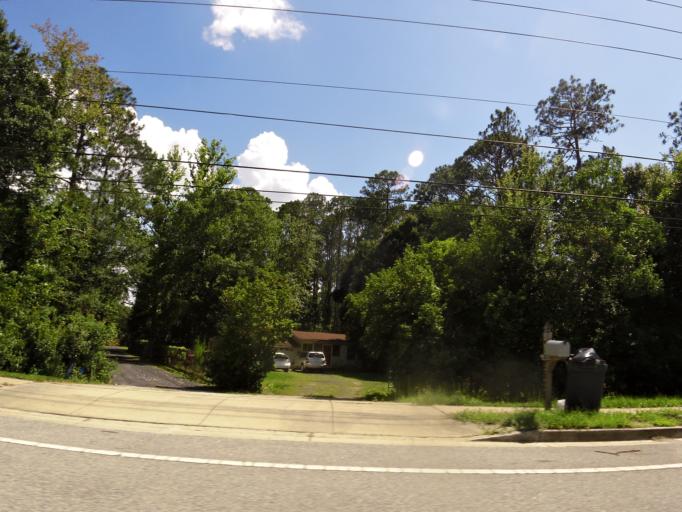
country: US
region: Florida
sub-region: Saint Johns County
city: Fruit Cove
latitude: 30.1494
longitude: -81.5784
